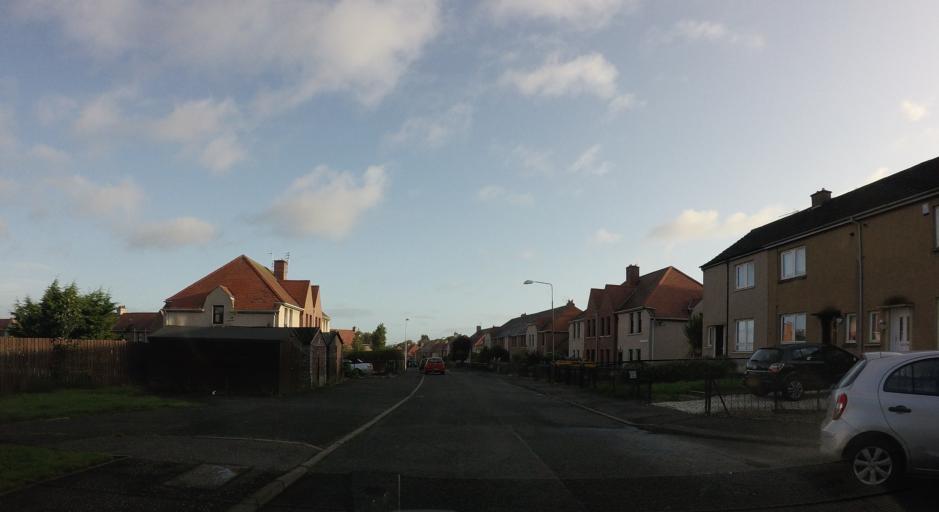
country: GB
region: Scotland
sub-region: East Lothian
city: Musselburgh
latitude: 55.9170
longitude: -3.0339
